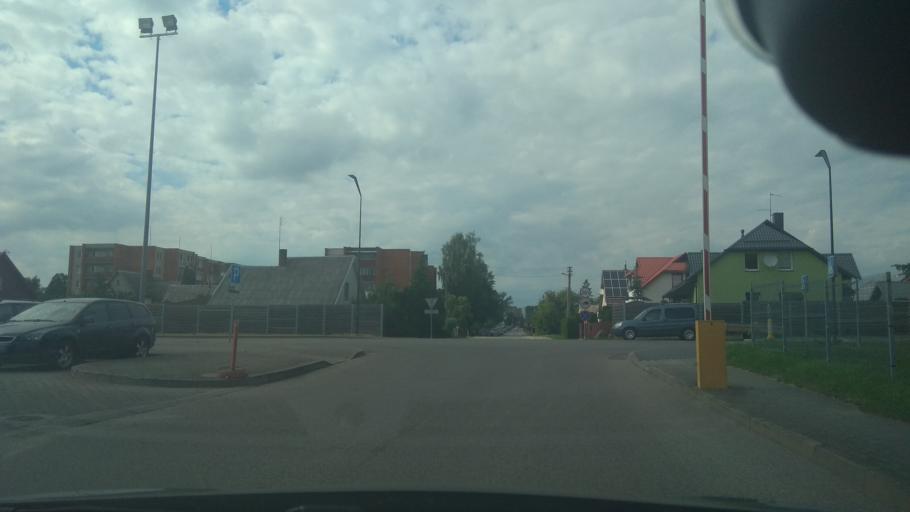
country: LT
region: Marijampoles apskritis
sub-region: Marijampole Municipality
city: Marijampole
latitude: 54.5380
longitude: 23.3488
